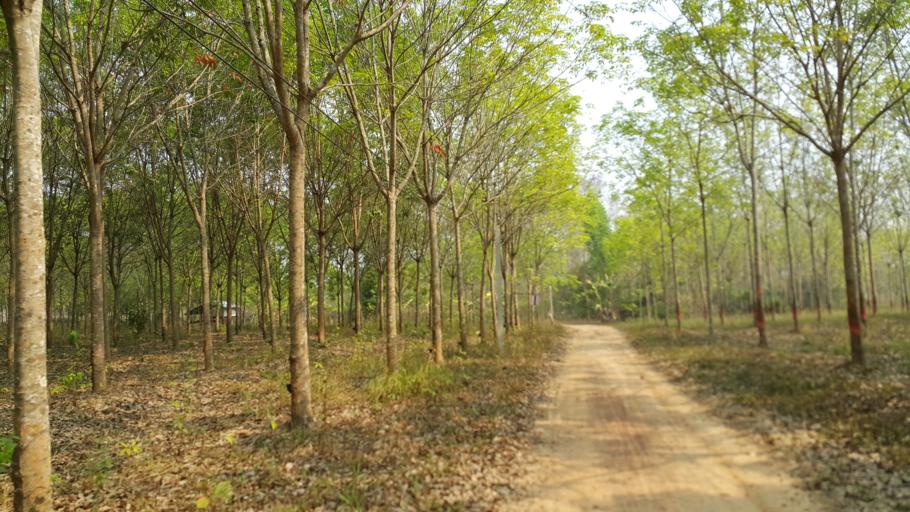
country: TH
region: Nakhon Phanom
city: Ban Phaeng
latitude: 17.8248
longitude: 104.2466
